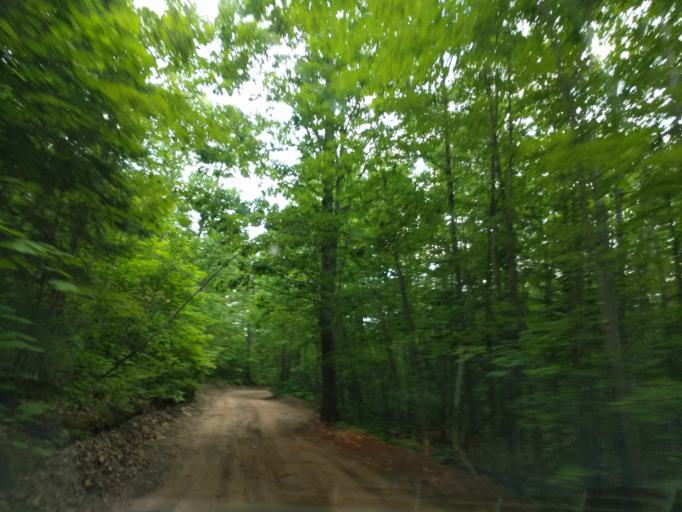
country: US
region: Michigan
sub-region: Marquette County
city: Trowbridge Park
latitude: 46.6123
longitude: -87.5093
